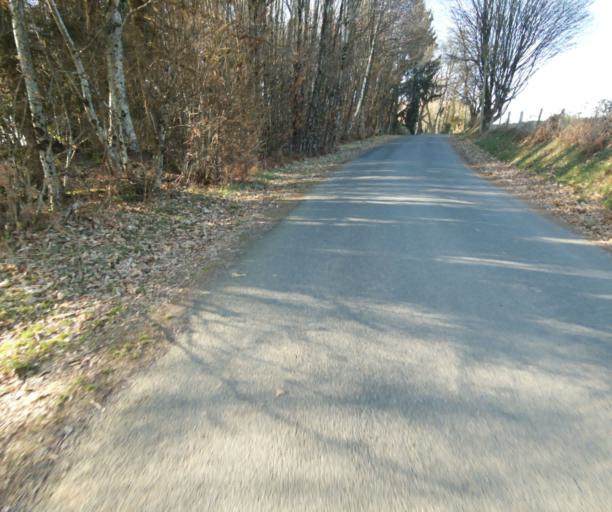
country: FR
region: Limousin
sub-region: Departement de la Correze
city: Seilhac
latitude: 45.3591
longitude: 1.7338
